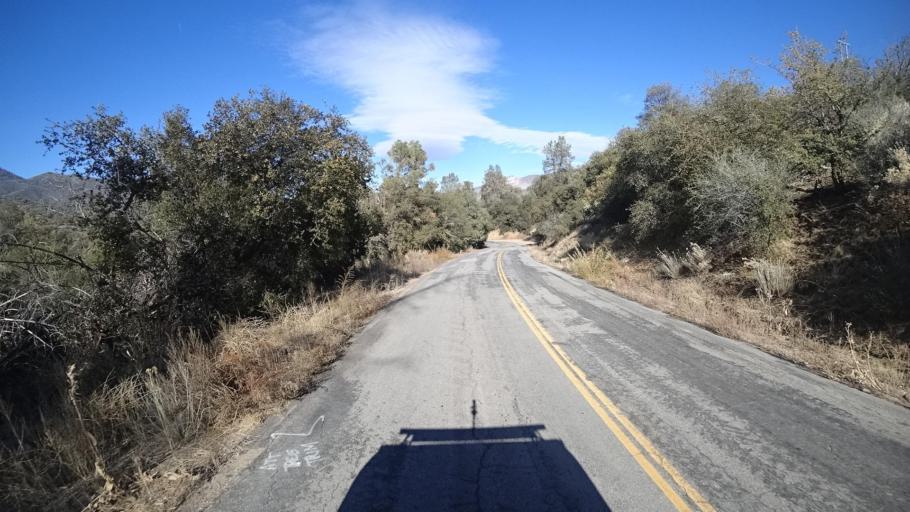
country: US
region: California
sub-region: Kern County
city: Bodfish
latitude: 35.4663
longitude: -118.5304
